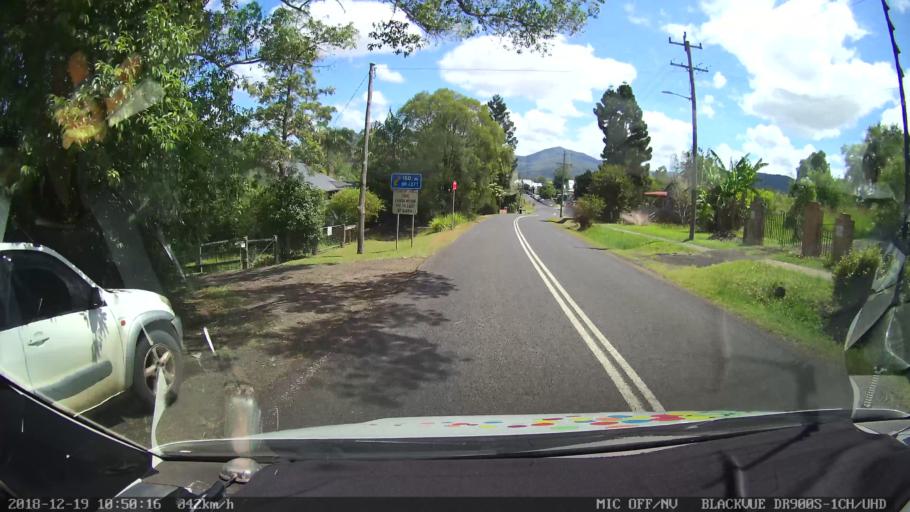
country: AU
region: New South Wales
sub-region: Lismore Municipality
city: Nimbin
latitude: -28.5988
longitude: 153.2222
